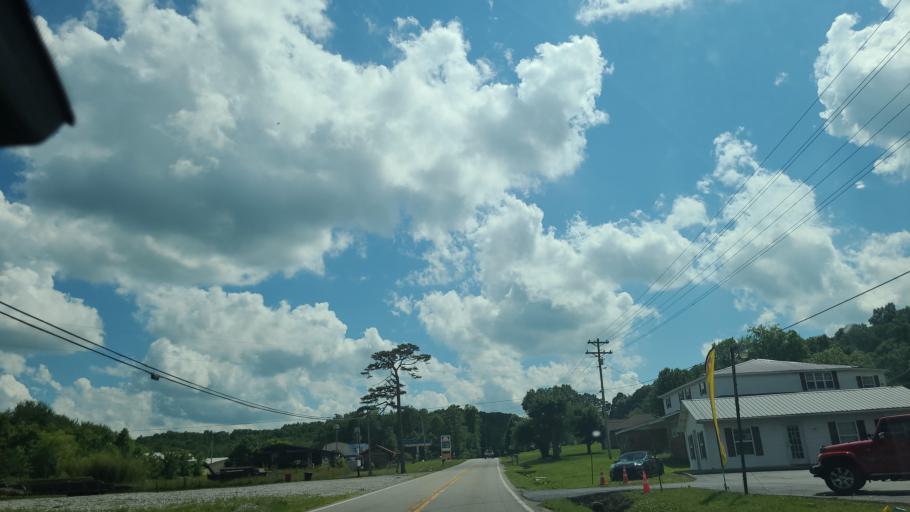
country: US
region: Kentucky
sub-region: Whitley County
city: Corbin
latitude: 36.8737
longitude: -84.2111
